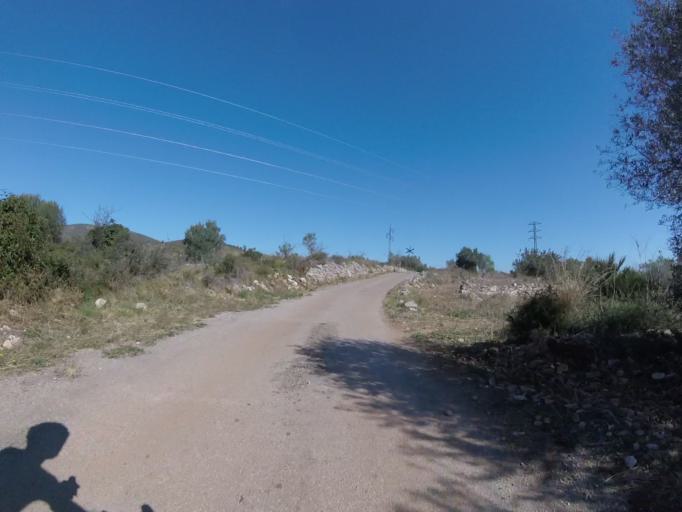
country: ES
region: Valencia
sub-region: Provincia de Castello
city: Santa Magdalena de Pulpis
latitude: 40.3499
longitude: 0.2779
